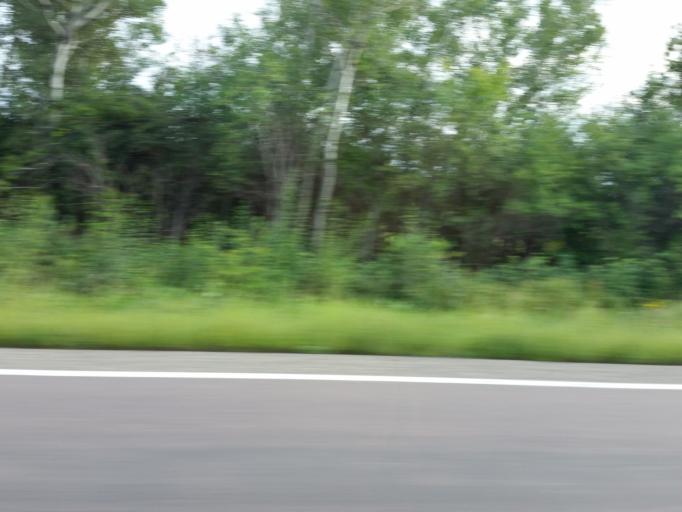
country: US
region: Minnesota
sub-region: Dakota County
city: Farmington
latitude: 44.6304
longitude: -93.0493
